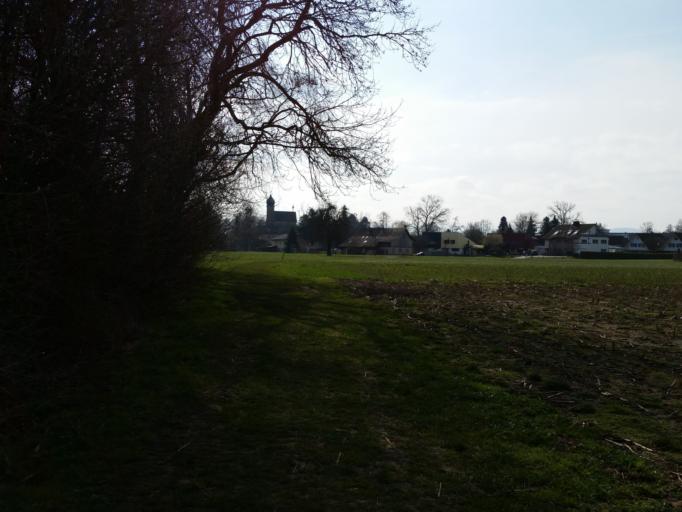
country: CH
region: Thurgau
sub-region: Arbon District
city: Egnach
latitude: 47.5510
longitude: 9.3810
